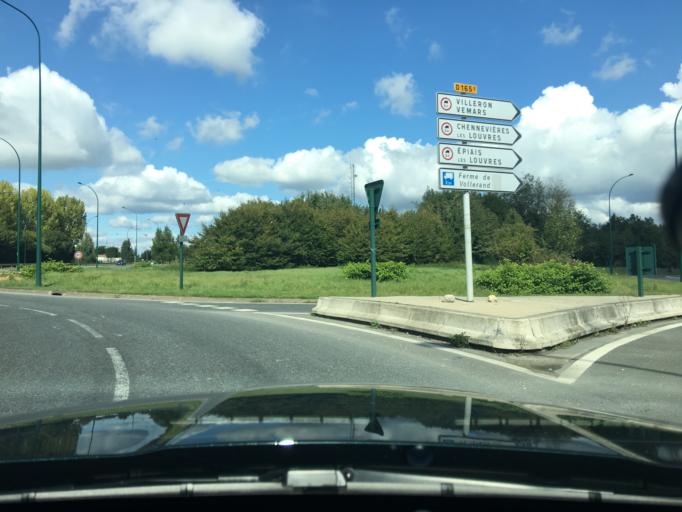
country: FR
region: Ile-de-France
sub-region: Departement du Val-d'Oise
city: Louvres
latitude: 49.0457
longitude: 2.5118
